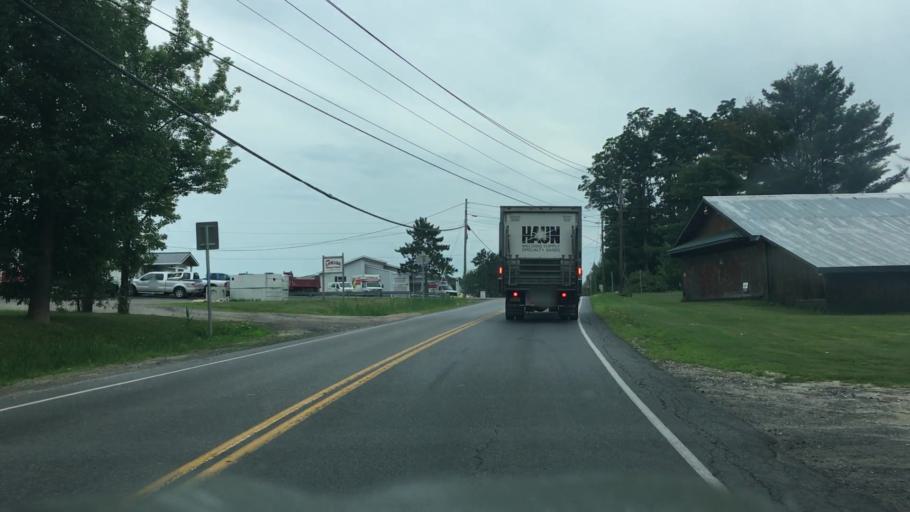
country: US
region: New York
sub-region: Clinton County
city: Plattsburgh West
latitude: 44.6670
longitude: -73.5075
